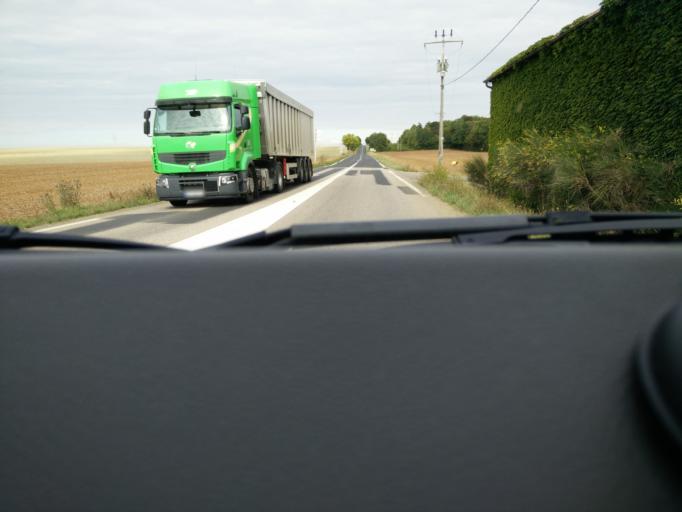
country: FR
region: Lorraine
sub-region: Departement de Meurthe-et-Moselle
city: Montauville
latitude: 48.8943
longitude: 5.9781
